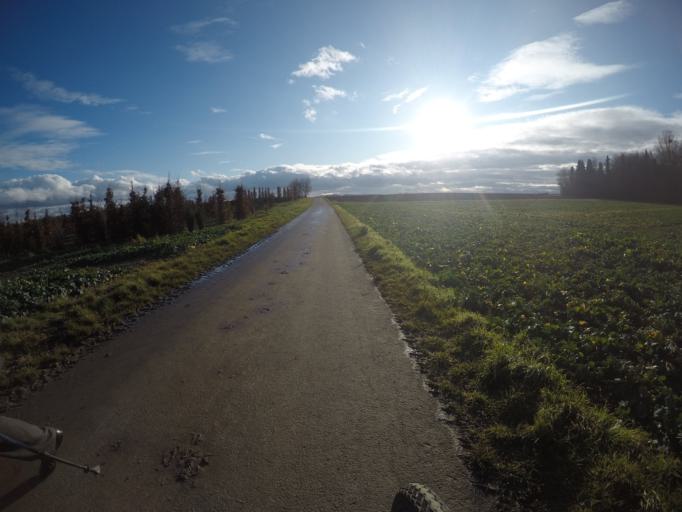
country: DE
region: Baden-Wuerttemberg
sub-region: Regierungsbezirk Stuttgart
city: Bondorf
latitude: 48.5419
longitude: 8.8741
